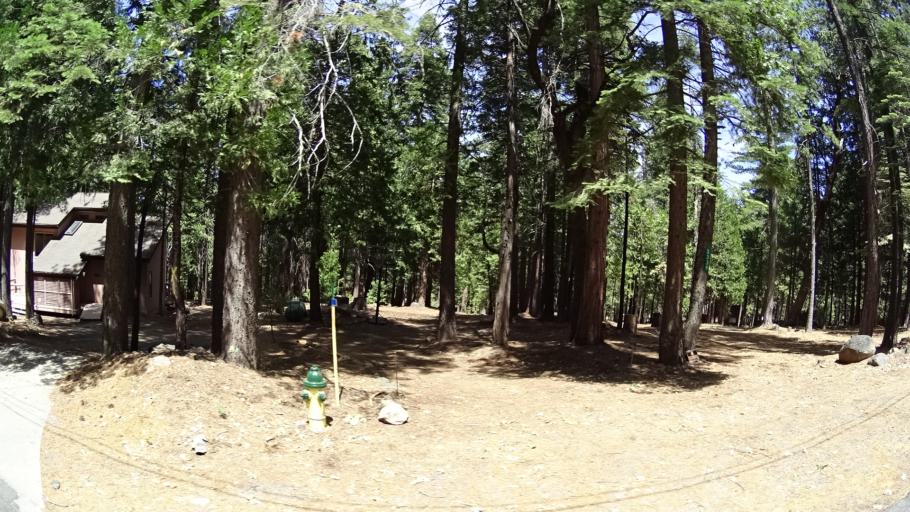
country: US
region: California
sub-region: Calaveras County
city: Arnold
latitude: 38.3087
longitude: -120.2629
